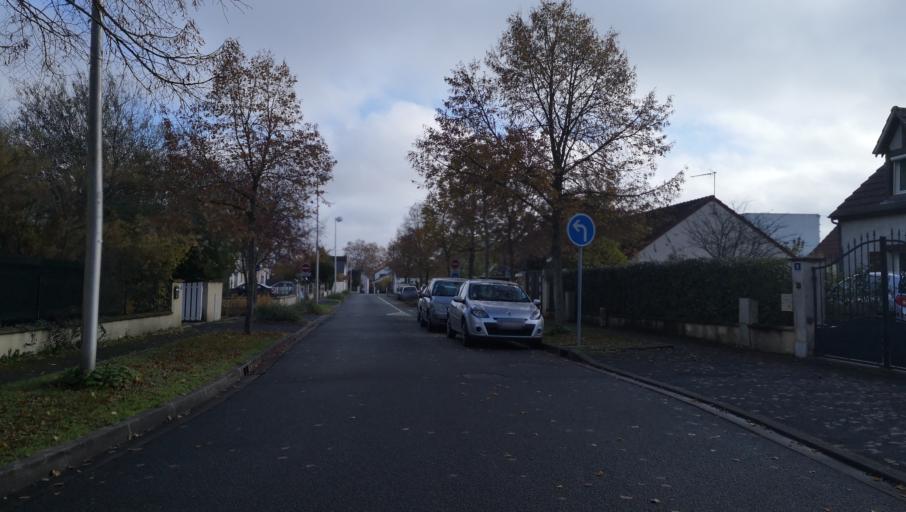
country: FR
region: Centre
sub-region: Departement du Loiret
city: Semoy
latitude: 47.9182
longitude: 1.9356
